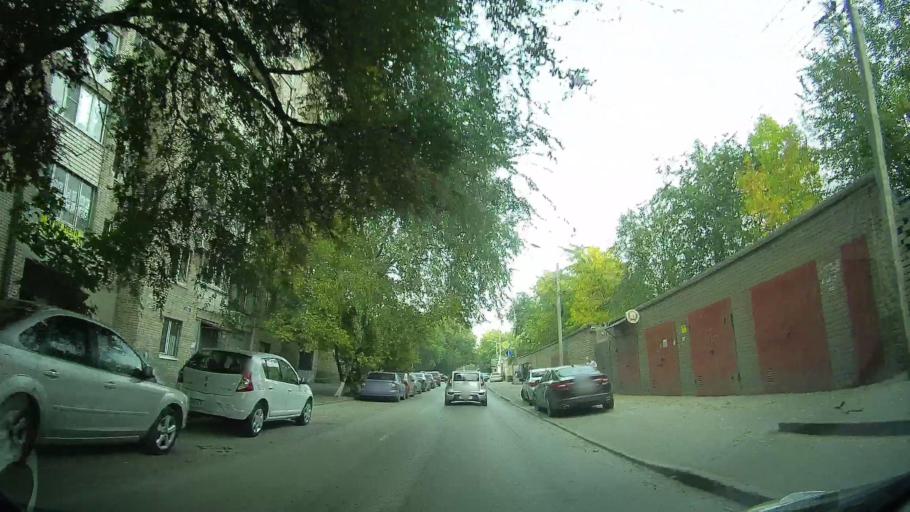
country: RU
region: Rostov
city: Rostov-na-Donu
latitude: 47.2348
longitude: 39.7183
